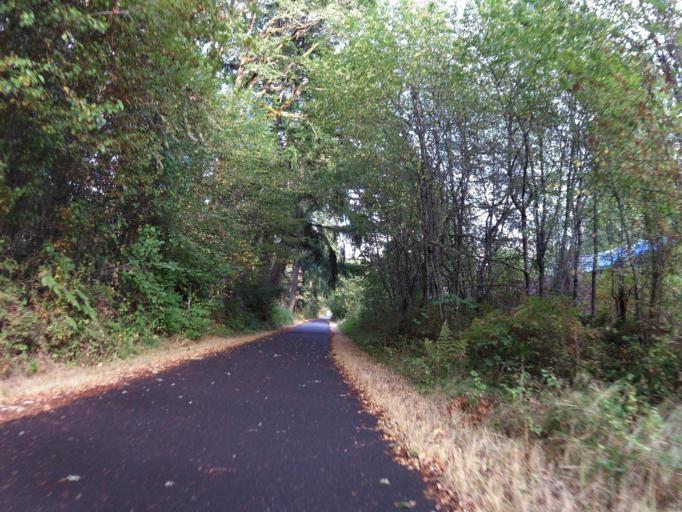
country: US
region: Washington
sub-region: Thurston County
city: Rainier
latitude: 46.9075
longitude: -122.7764
